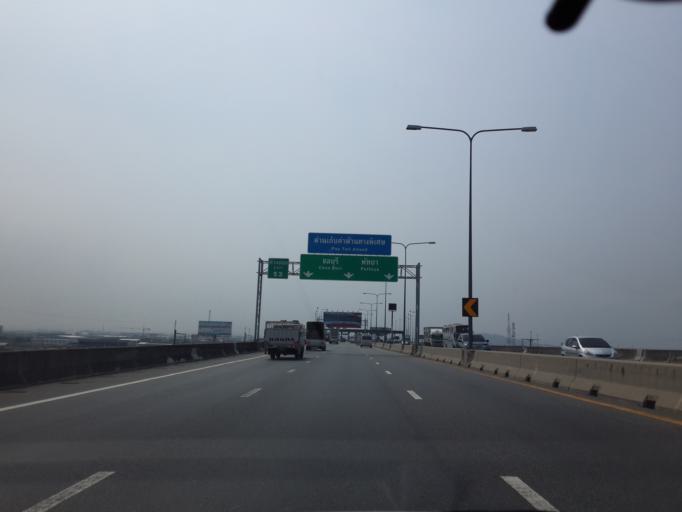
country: TH
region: Chachoengsao
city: Bang Pakong
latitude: 13.4612
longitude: 100.9960
